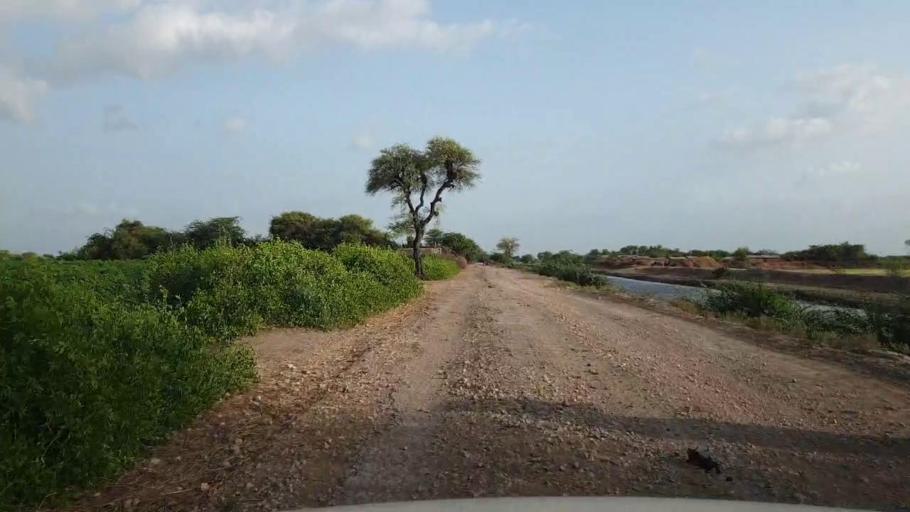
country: PK
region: Sindh
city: Kario
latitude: 24.8021
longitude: 68.6473
